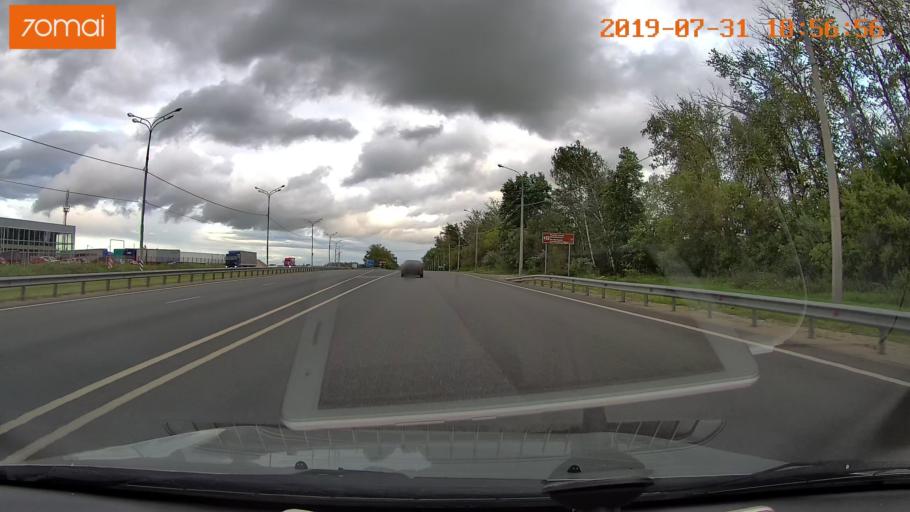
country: RU
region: Moskovskaya
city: Raduzhnyy
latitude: 55.1584
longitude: 38.6852
